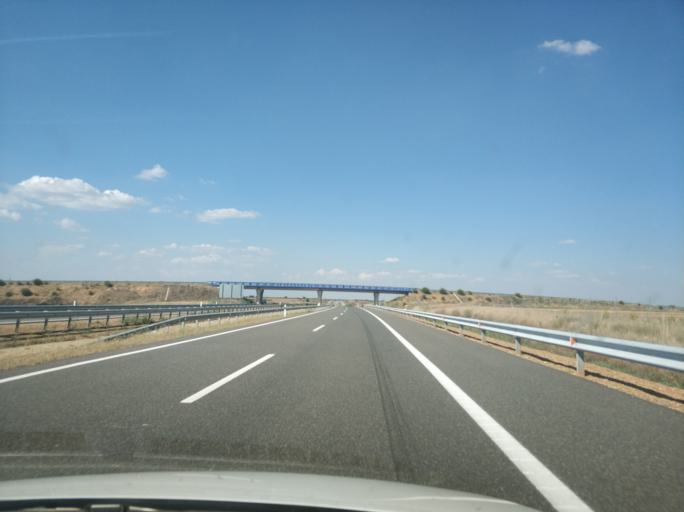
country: ES
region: Castille and Leon
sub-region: Provincia de Zamora
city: Santovenia
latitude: 41.8760
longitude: -5.7000
